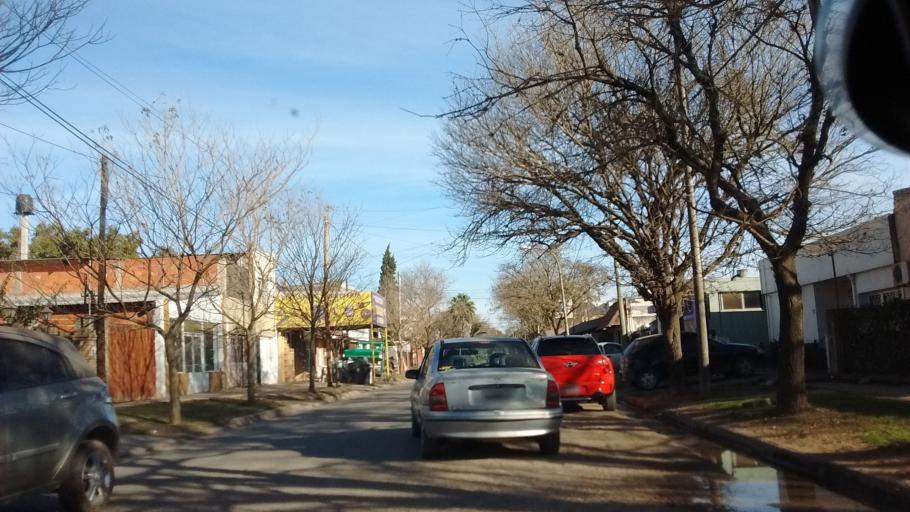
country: AR
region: Santa Fe
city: Funes
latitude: -32.9122
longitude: -60.8125
